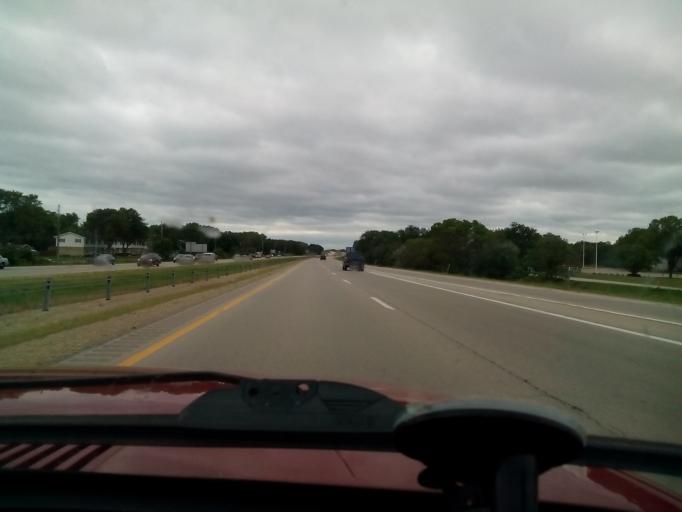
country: US
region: Wisconsin
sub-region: Dane County
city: Sun Prairie
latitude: 43.1855
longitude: -89.2360
